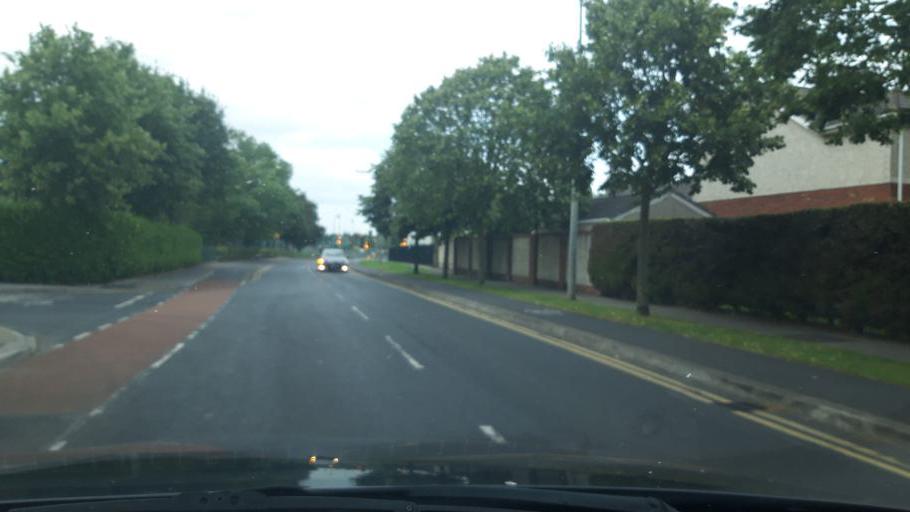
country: IE
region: Leinster
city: Hartstown
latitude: 53.4023
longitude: -6.4259
